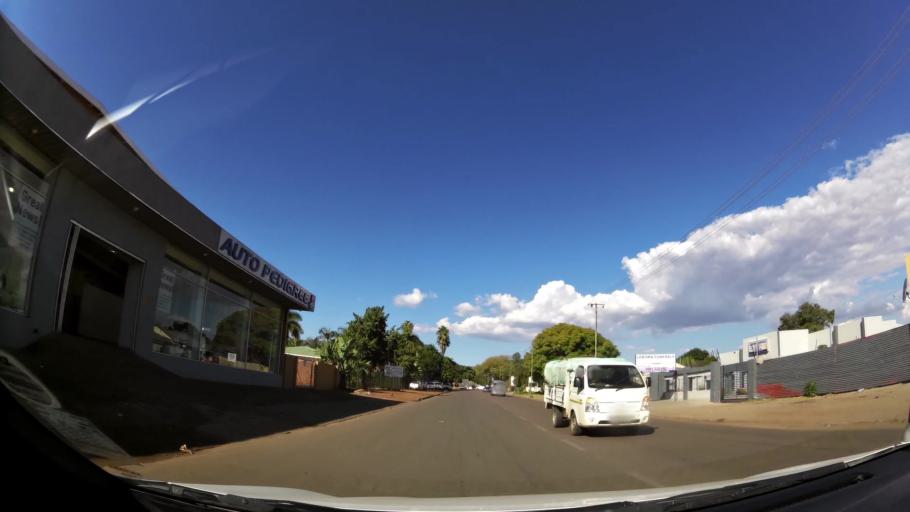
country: ZA
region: Limpopo
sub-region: Waterberg District Municipality
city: Mokopane
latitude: -24.1771
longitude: 29.0111
